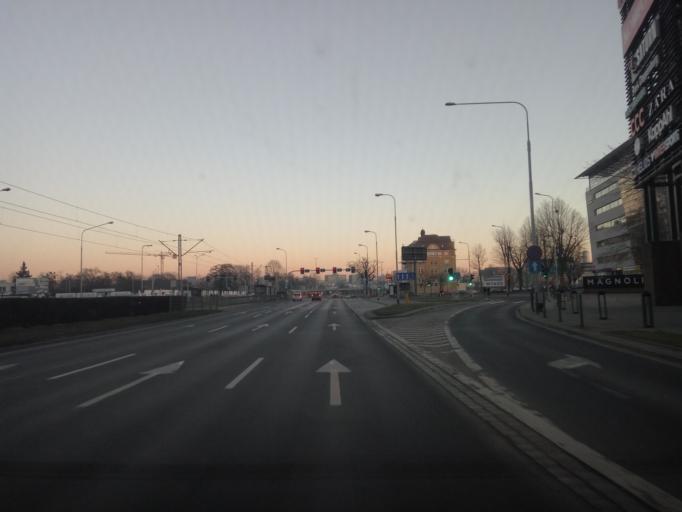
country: PL
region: Lower Silesian Voivodeship
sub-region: Powiat wroclawski
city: Wroclaw
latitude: 51.1218
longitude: 16.9922
